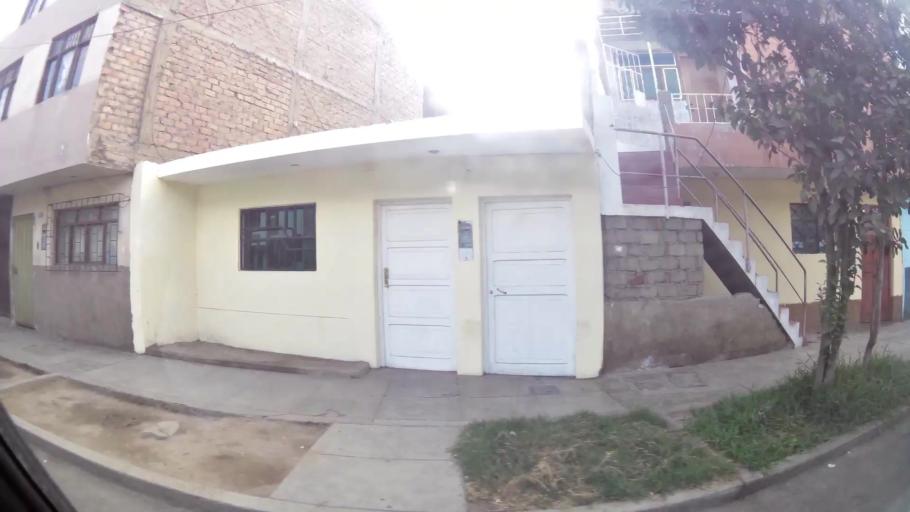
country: PE
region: La Libertad
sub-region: Provincia de Trujillo
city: Trujillo
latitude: -8.1036
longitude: -79.0140
